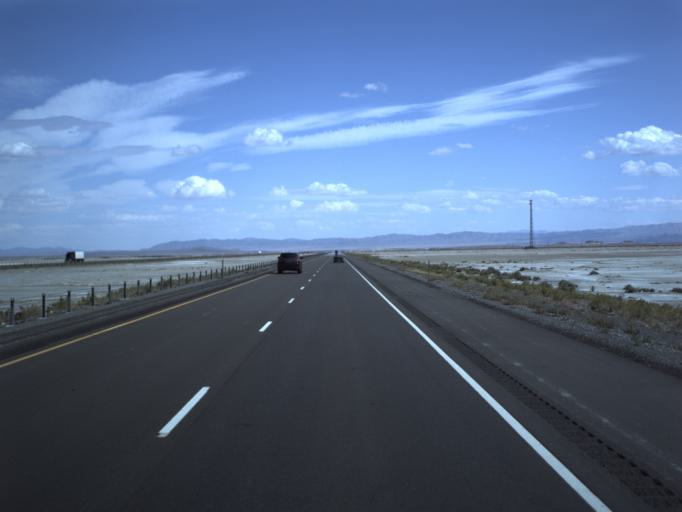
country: US
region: Utah
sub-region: Tooele County
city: Wendover
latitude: 40.7277
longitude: -113.3492
